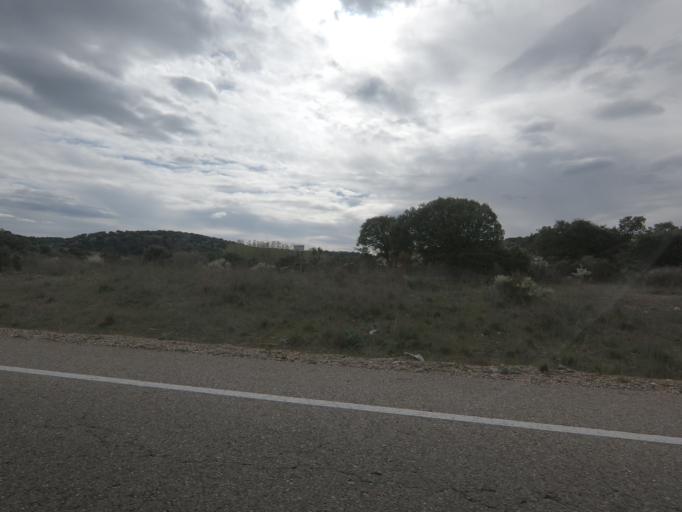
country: ES
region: Castille and Leon
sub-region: Provincia de Salamanca
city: Pastores
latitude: 40.5030
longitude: -6.5759
